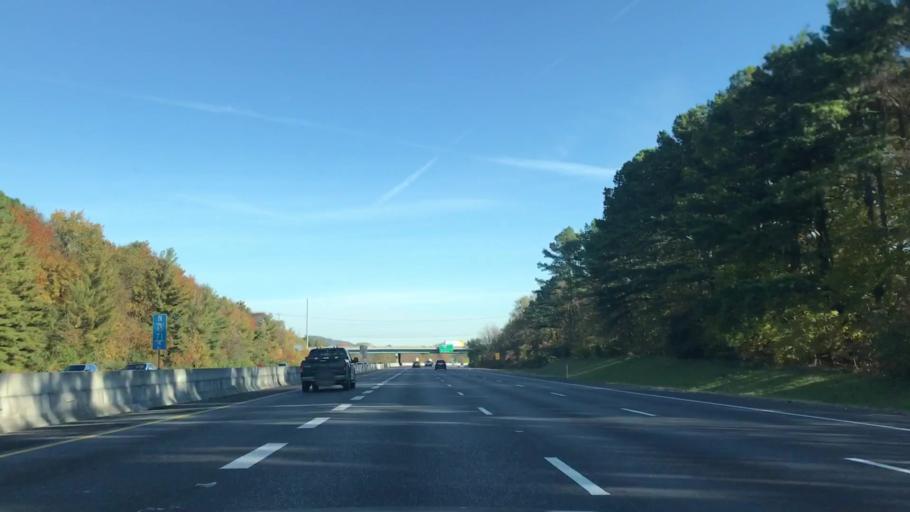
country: US
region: Tennessee
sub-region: Williamson County
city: Brentwood Estates
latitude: 35.9946
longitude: -86.7978
